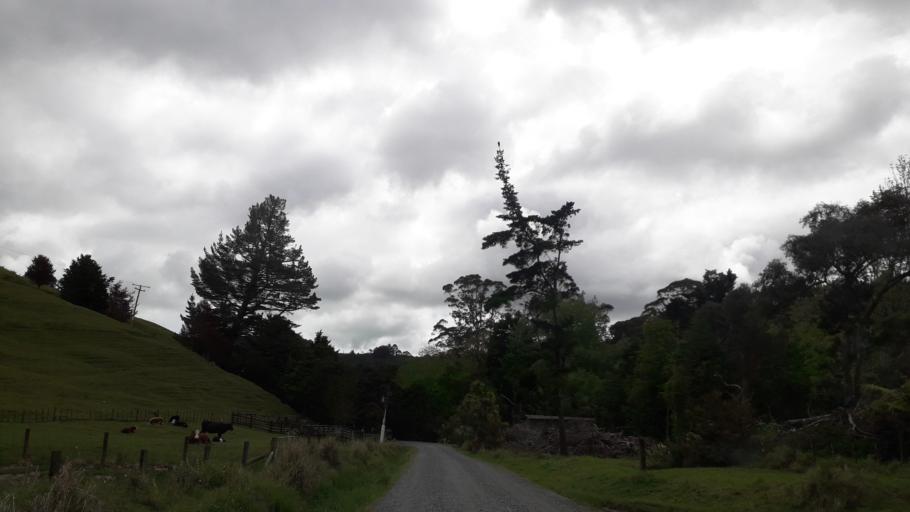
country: NZ
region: Northland
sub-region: Far North District
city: Taipa
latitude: -35.0699
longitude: 173.5543
